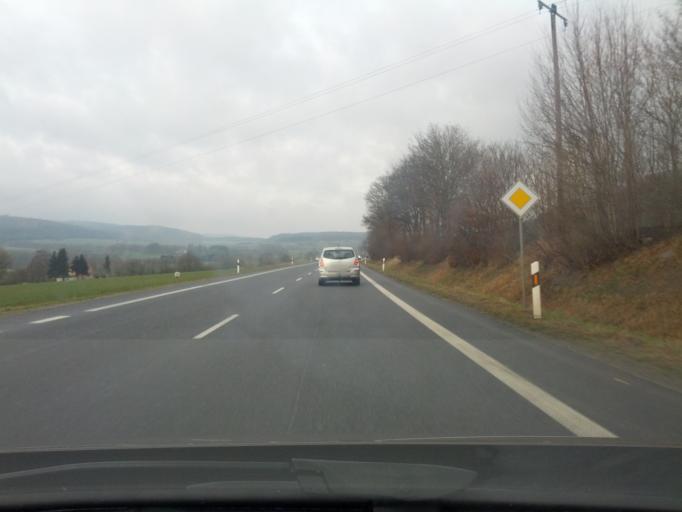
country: DE
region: Hesse
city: Witzenhausen
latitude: 51.3630
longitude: 9.8234
